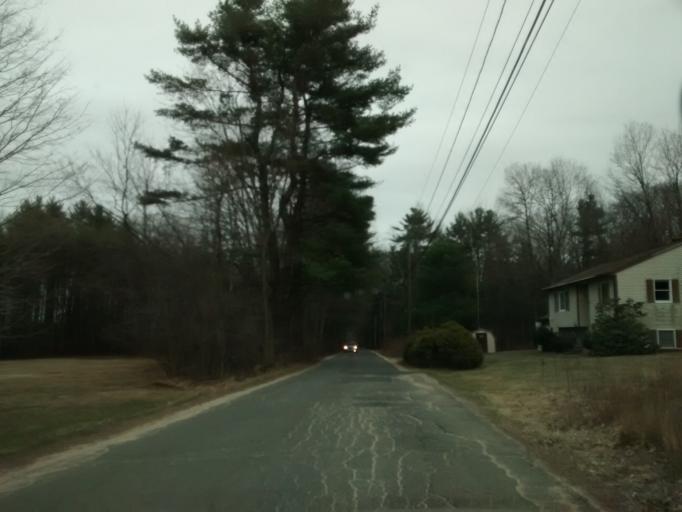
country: US
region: Massachusetts
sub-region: Franklin County
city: Orange
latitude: 42.5501
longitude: -72.2974
